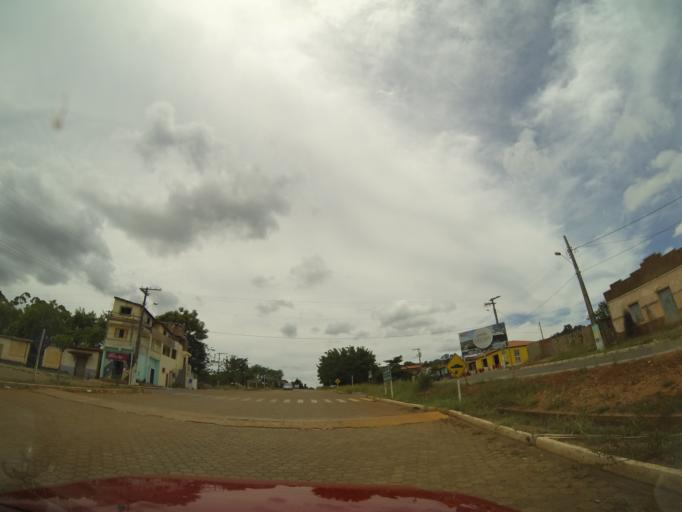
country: BR
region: Minas Gerais
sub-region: Turmalina
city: Turmalina
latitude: -17.1332
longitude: -42.7705
